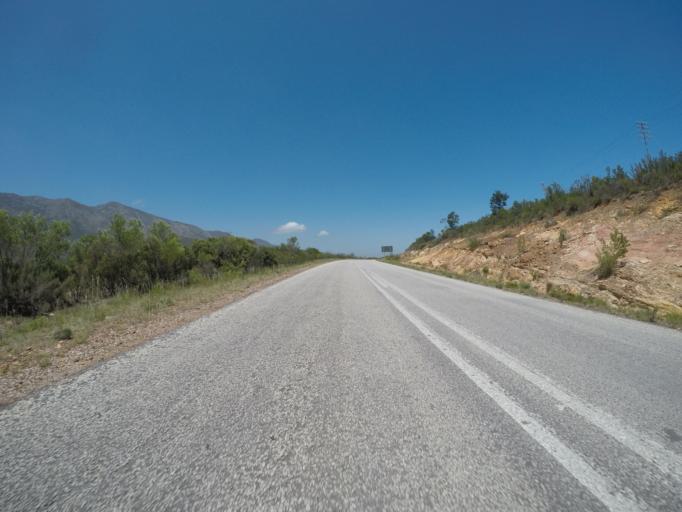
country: ZA
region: Eastern Cape
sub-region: Cacadu District Municipality
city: Kareedouw
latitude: -33.9101
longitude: 24.1635
